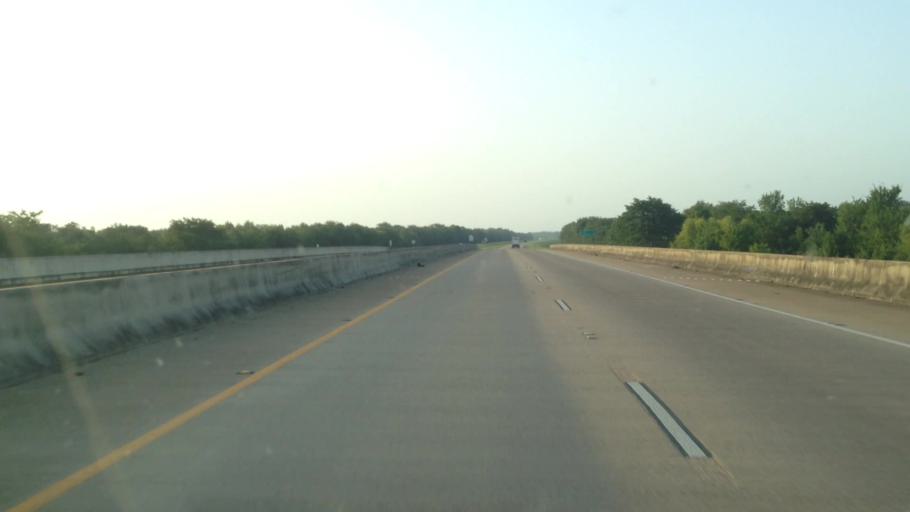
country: US
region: Louisiana
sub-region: Natchitoches Parish
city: Vienna Bend
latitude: 31.5971
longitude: -93.0384
